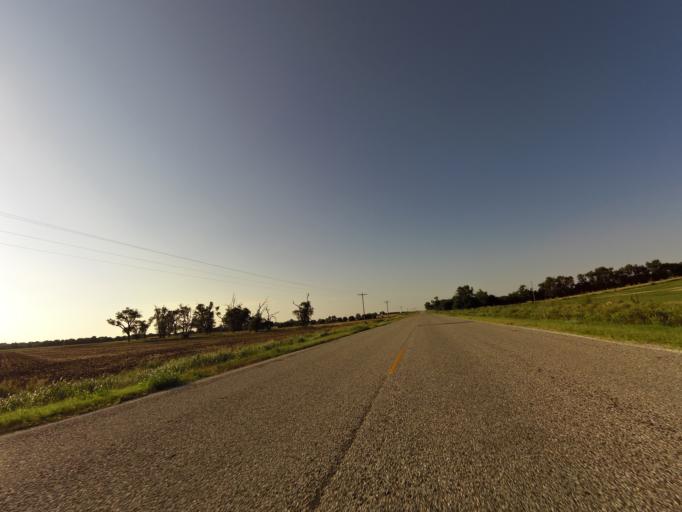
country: US
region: Kansas
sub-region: Reno County
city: Buhler
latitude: 38.1765
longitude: -97.8486
